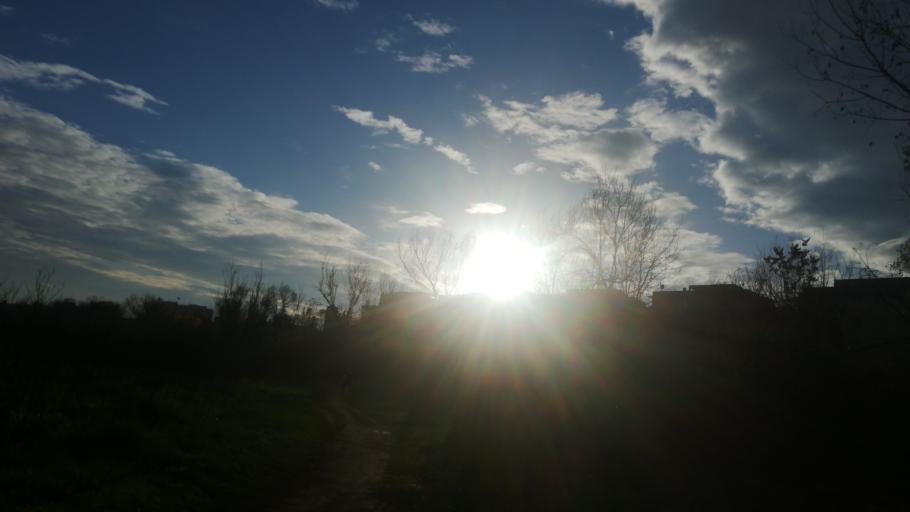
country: IT
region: Latium
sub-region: Citta metropolitana di Roma Capitale
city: Rome
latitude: 41.9314
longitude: 12.5304
